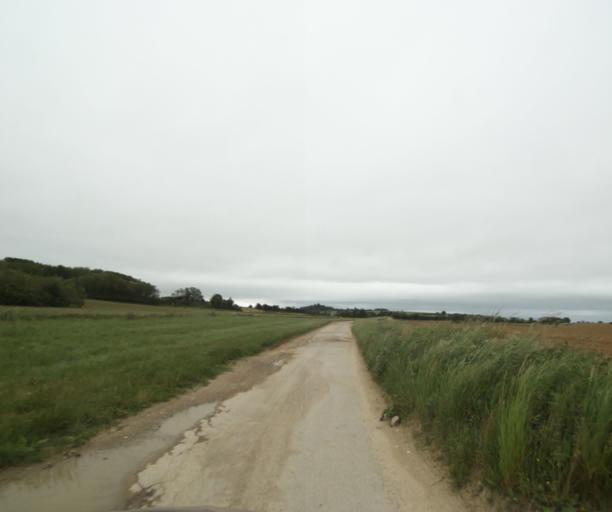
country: FR
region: Rhone-Alpes
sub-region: Departement de l'Ain
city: Miribel
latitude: 45.8443
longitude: 4.9338
